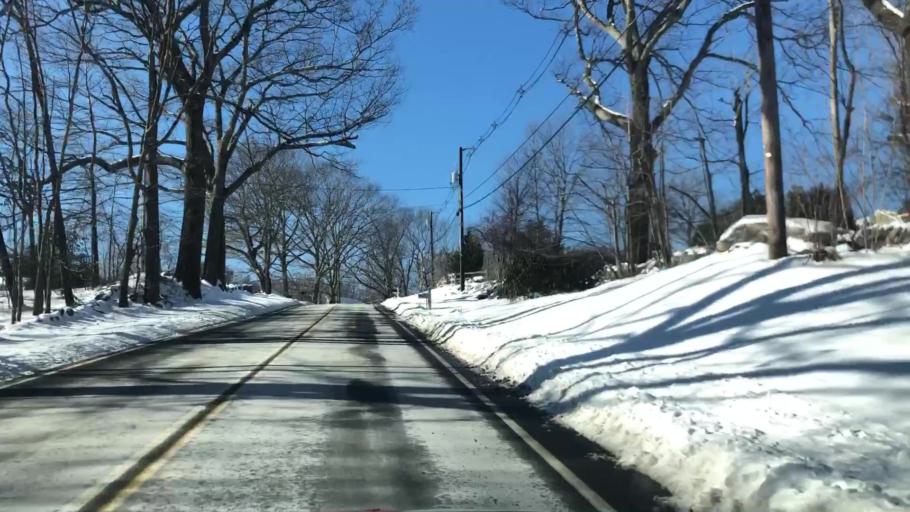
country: US
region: New Hampshire
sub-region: Hillsborough County
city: Bedford
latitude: 42.9407
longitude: -71.5399
